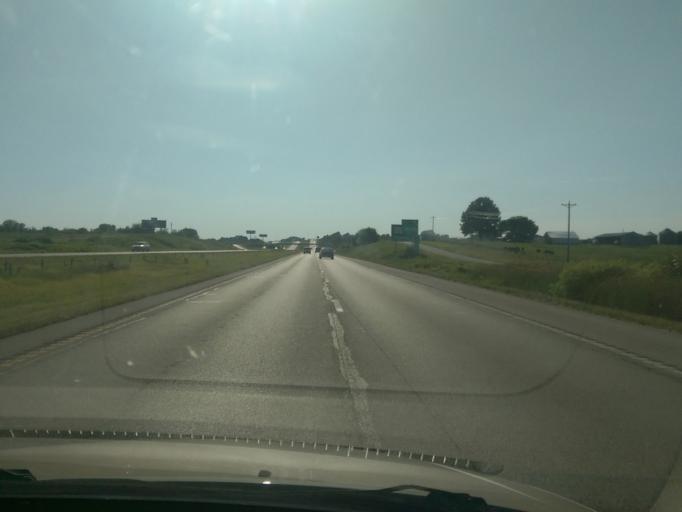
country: US
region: Missouri
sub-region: Lafayette County
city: Odessa
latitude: 39.0075
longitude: -93.9343
